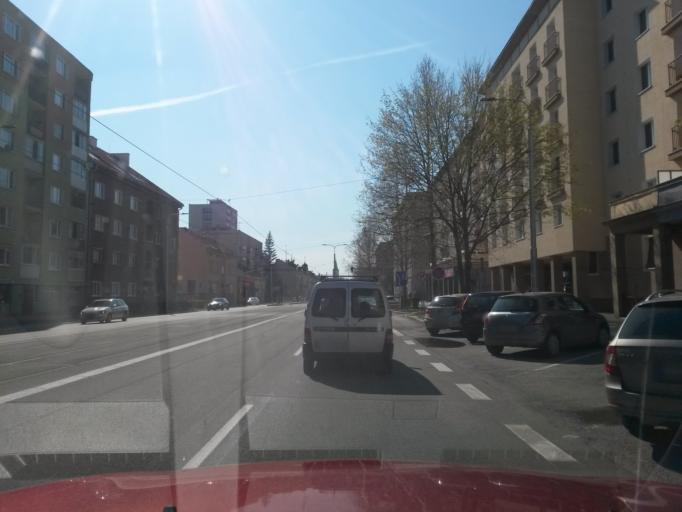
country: SK
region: Kosicky
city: Kosice
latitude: 48.7305
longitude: 21.2509
